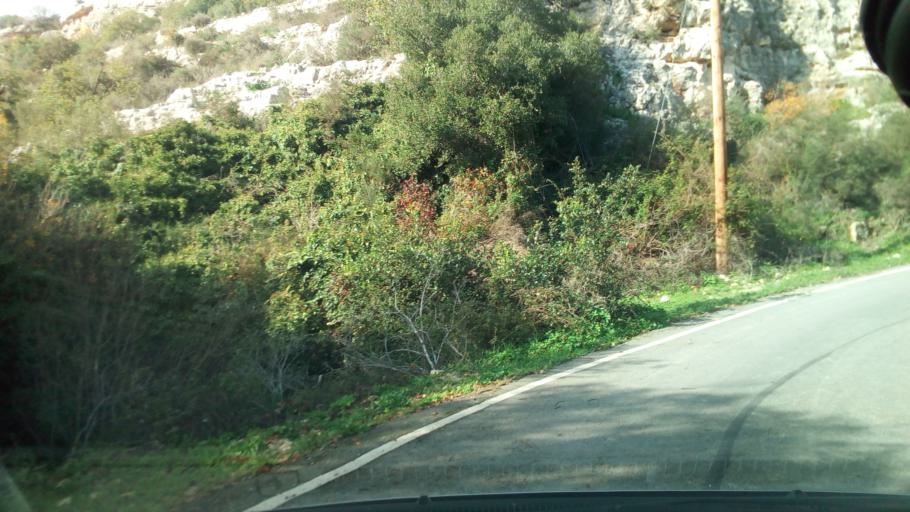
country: CY
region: Pafos
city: Polis
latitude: 34.9531
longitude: 32.4270
